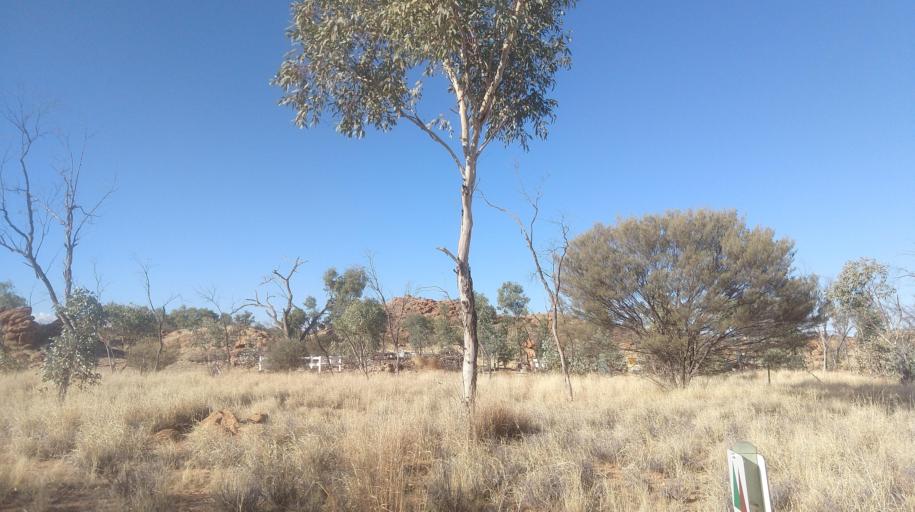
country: AU
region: Northern Territory
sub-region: Alice Springs
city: Alice Springs
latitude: -23.6703
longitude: 133.8851
